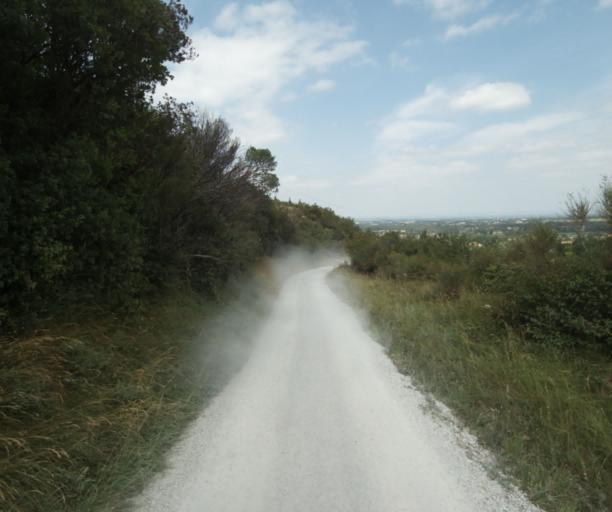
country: FR
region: Midi-Pyrenees
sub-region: Departement du Tarn
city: Soreze
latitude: 43.4420
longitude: 2.0437
